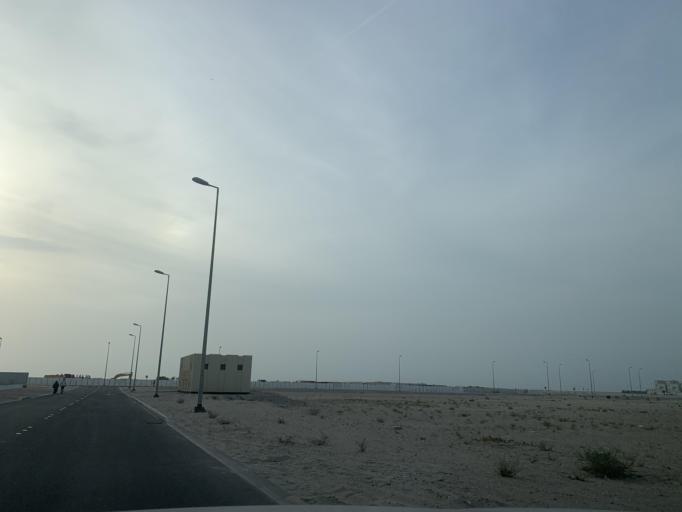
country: BH
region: Muharraq
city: Al Muharraq
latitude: 26.3099
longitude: 50.6196
